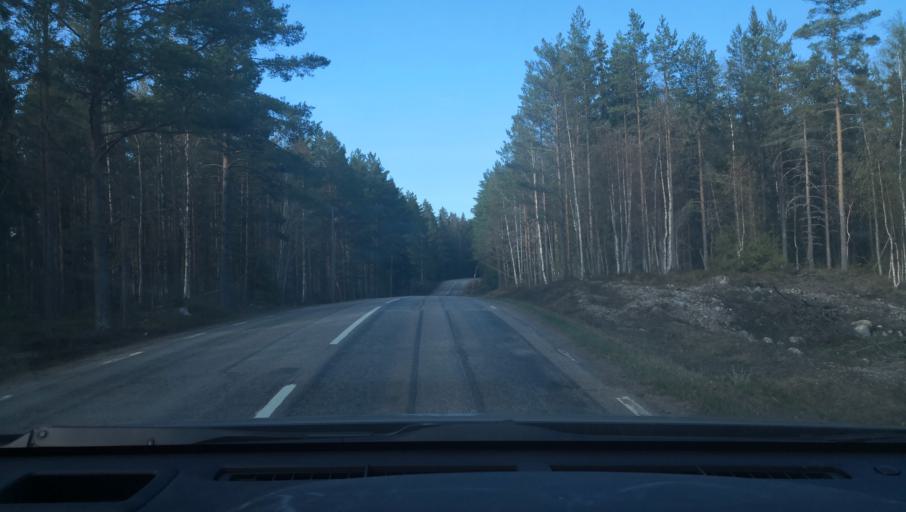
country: SE
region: Uppsala
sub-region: Heby Kommun
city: Morgongava
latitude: 59.9977
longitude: 16.9270
